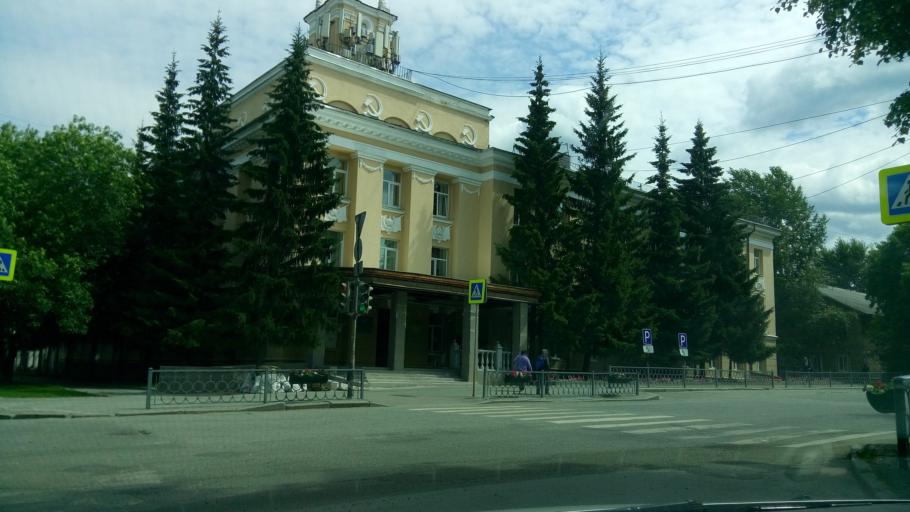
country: RU
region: Sverdlovsk
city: Yekaterinburg
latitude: 56.8871
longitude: 60.6237
